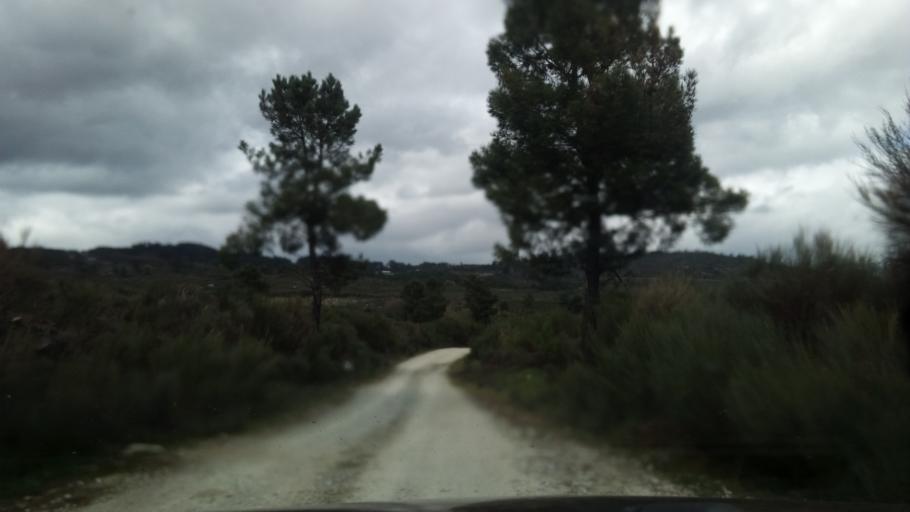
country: PT
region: Guarda
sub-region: Fornos de Algodres
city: Fornos de Algodres
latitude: 40.5972
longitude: -7.5686
